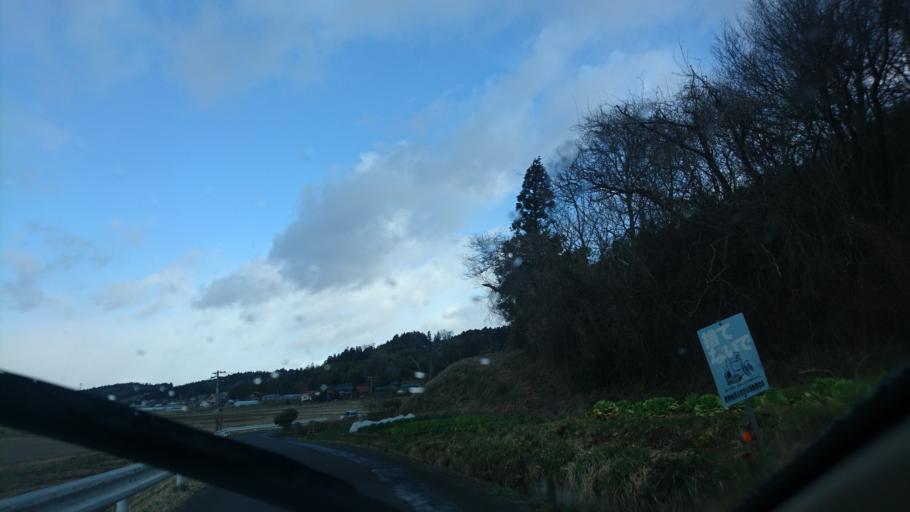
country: JP
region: Iwate
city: Ichinoseki
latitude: 38.7874
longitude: 141.0349
